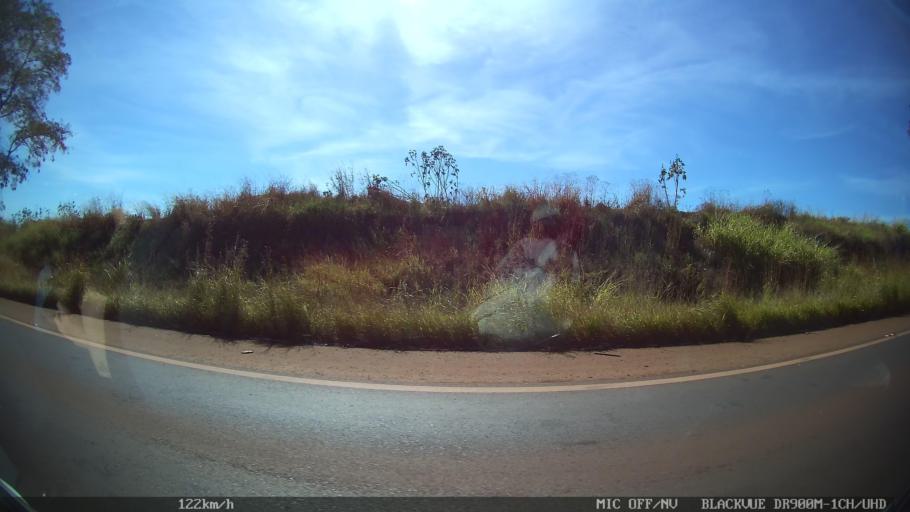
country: BR
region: Sao Paulo
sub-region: Sao Joaquim Da Barra
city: Sao Joaquim da Barra
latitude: -20.5544
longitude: -47.7219
